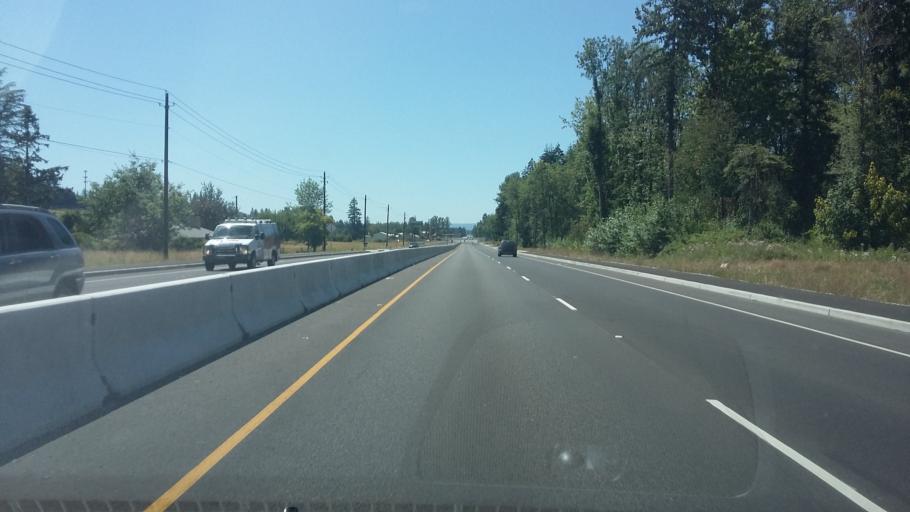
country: US
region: Washington
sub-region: Clark County
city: Meadow Glade
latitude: 45.7805
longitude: -122.5699
